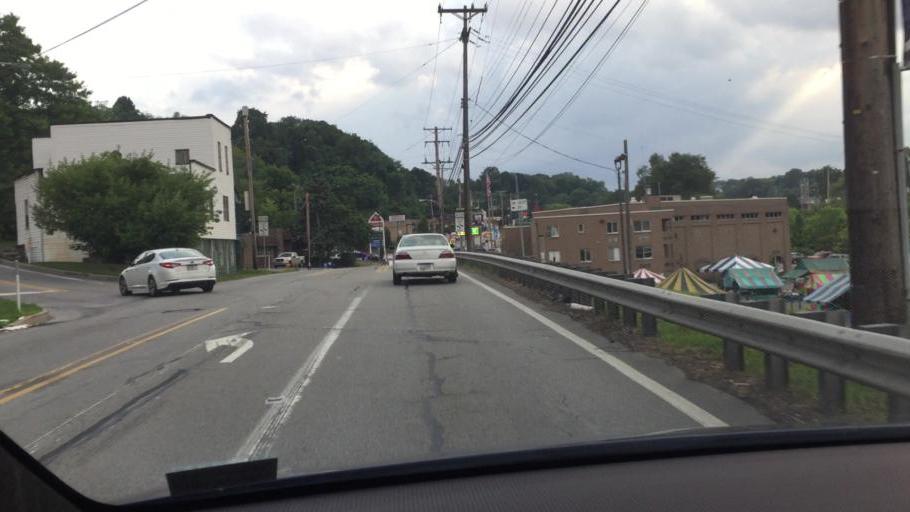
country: US
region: Pennsylvania
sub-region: Allegheny County
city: Castle Shannon
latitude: 40.3660
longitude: -80.0162
